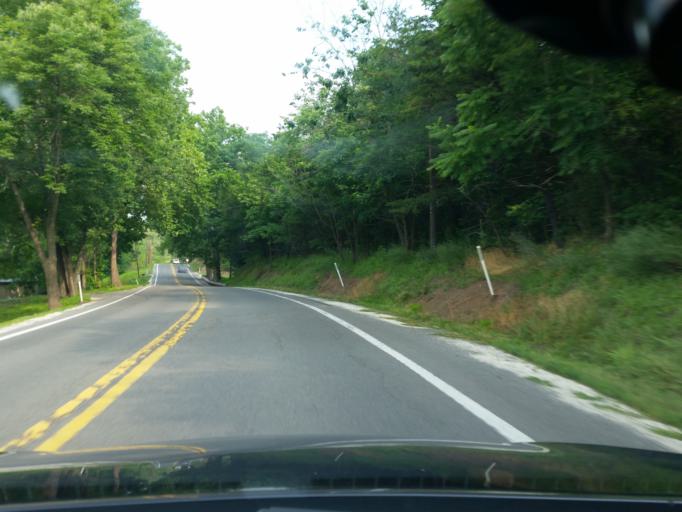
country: US
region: Pennsylvania
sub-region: Perry County
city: New Bloomfield
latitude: 40.3404
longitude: -77.1852
